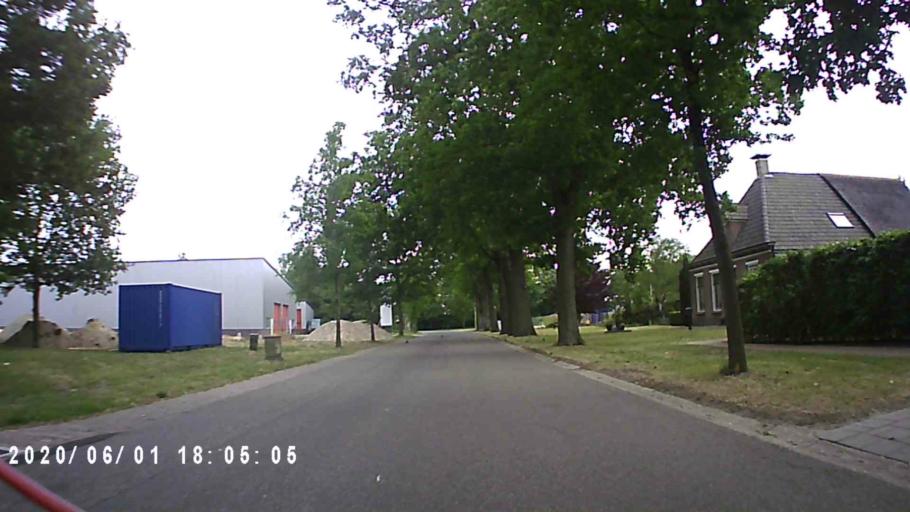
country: NL
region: Friesland
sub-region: Gemeente Tytsjerksteradiel
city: Sumar
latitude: 53.1805
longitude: 5.9941
